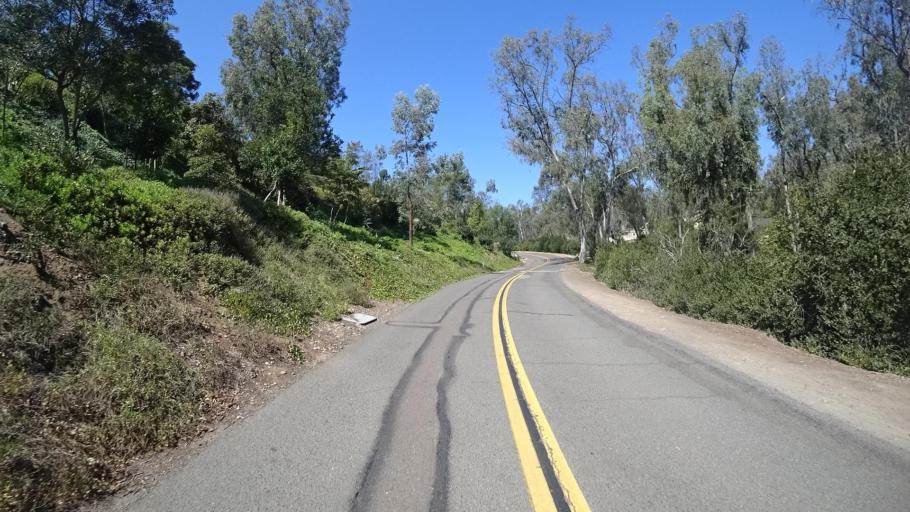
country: US
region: California
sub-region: San Diego County
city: Rancho Santa Fe
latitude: 33.0020
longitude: -117.2199
